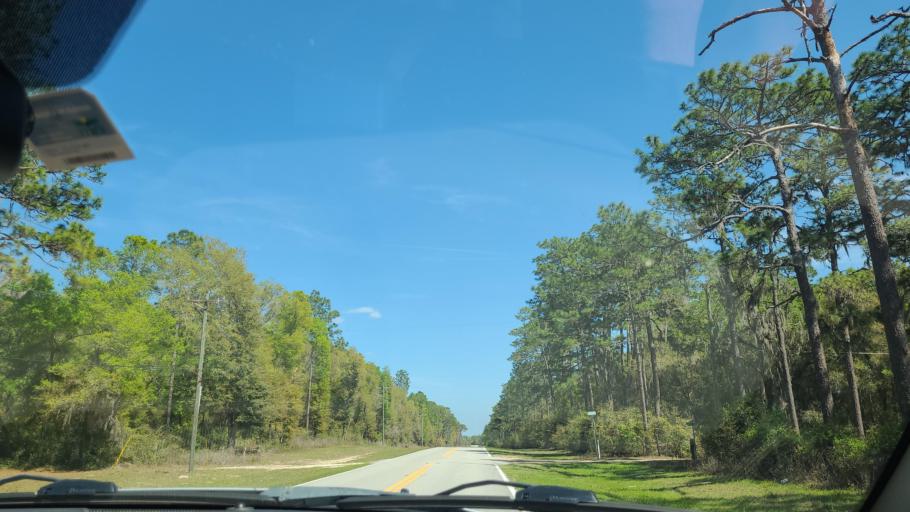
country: US
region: Florida
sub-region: Putnam County
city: Interlachen
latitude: 29.3780
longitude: -81.7875
